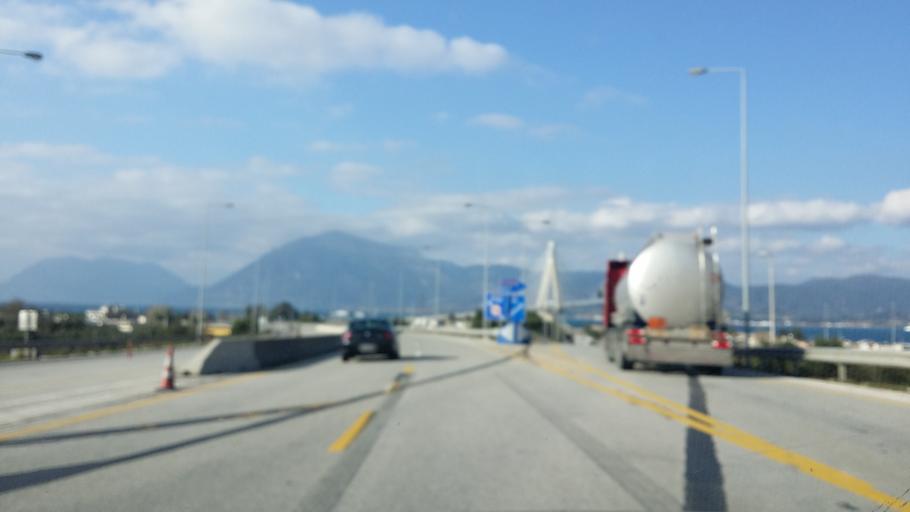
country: GR
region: West Greece
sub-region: Nomos Achaias
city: Rio
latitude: 38.3035
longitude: 21.7878
